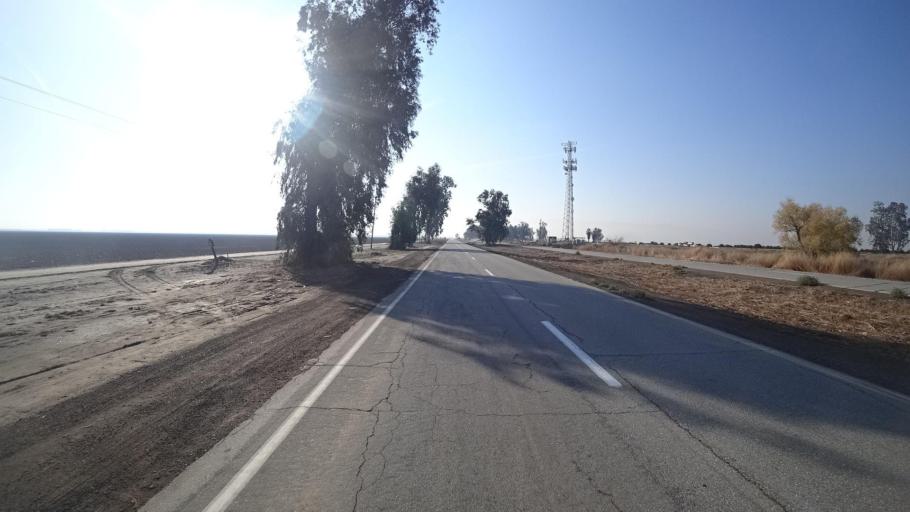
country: US
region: California
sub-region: Kern County
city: Greenfield
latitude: 35.1785
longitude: -119.0031
